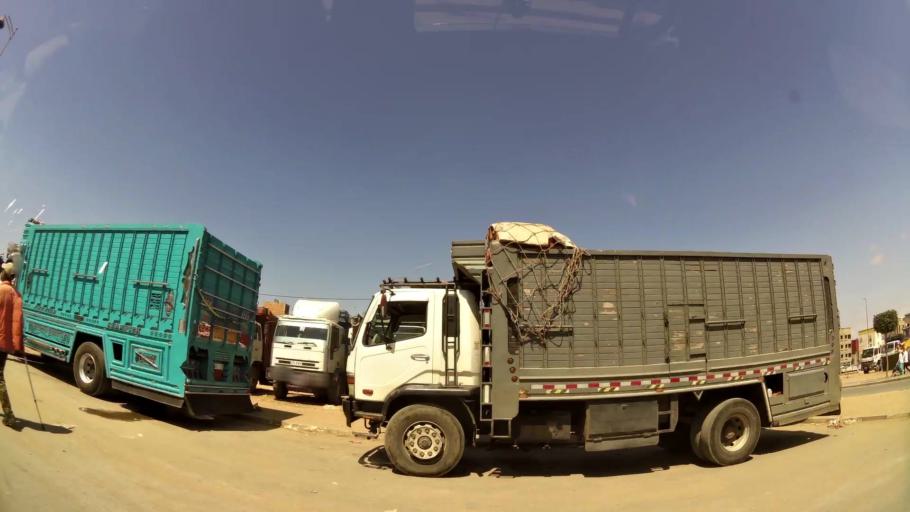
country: MA
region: Gharb-Chrarda-Beni Hssen
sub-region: Kenitra Province
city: Kenitra
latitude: 34.2409
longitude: -6.5481
